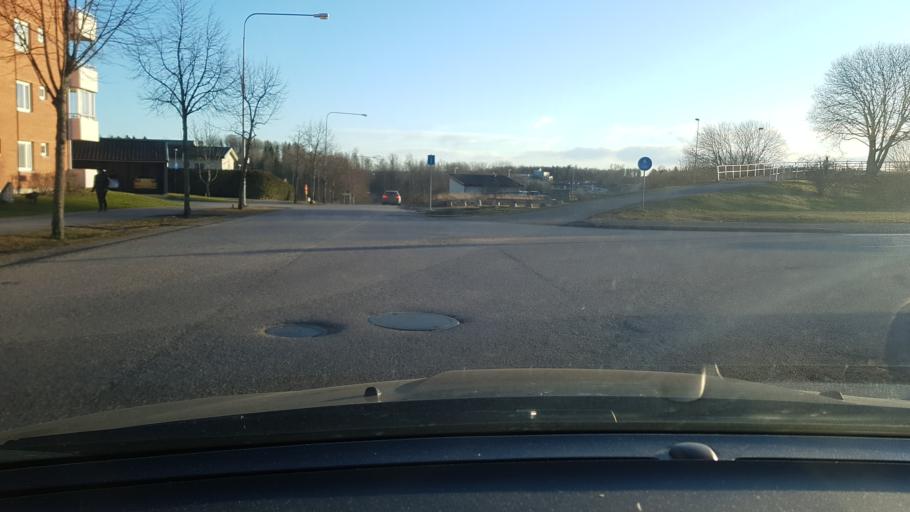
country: SE
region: Stockholm
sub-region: Norrtalje Kommun
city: Norrtalje
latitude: 59.7468
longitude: 18.6923
